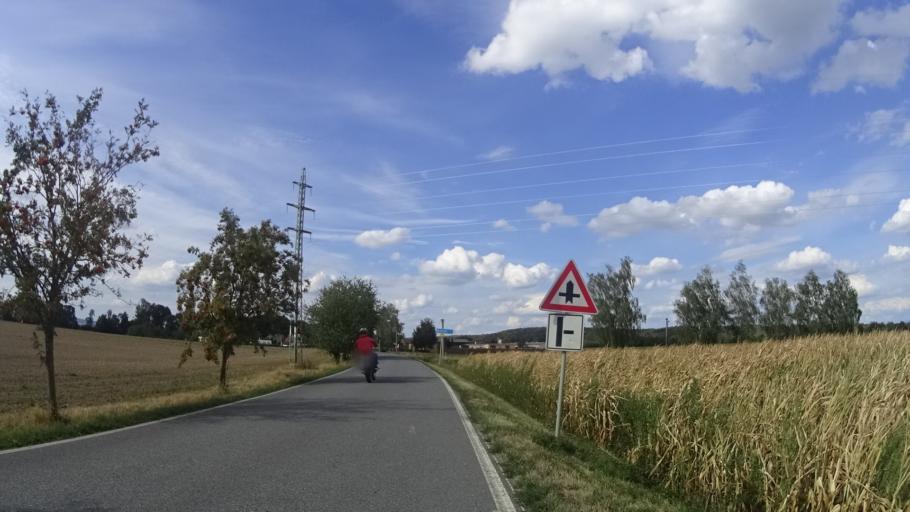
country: CZ
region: Olomoucky
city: Moravicany
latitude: 49.7400
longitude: 16.9741
